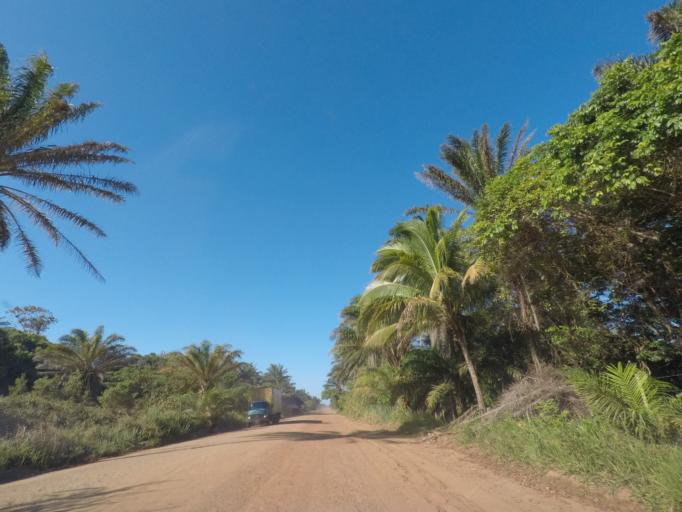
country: BR
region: Bahia
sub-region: Marau
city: Marau
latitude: -14.0616
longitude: -38.9576
